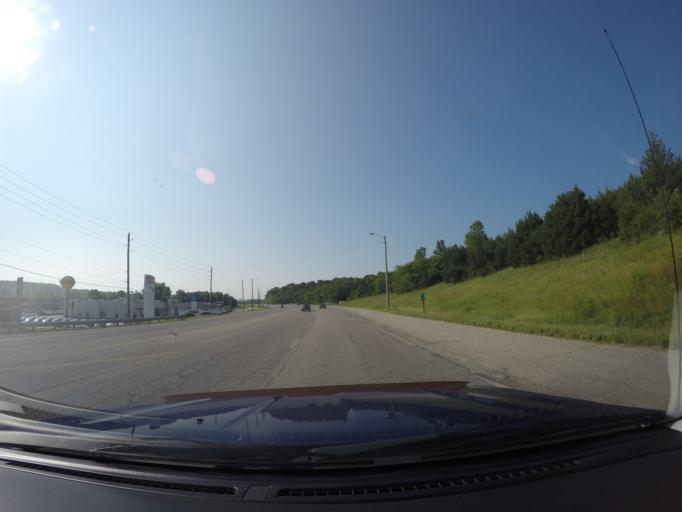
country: US
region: Kansas
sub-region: Riley County
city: Manhattan
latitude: 39.1823
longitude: -96.6101
